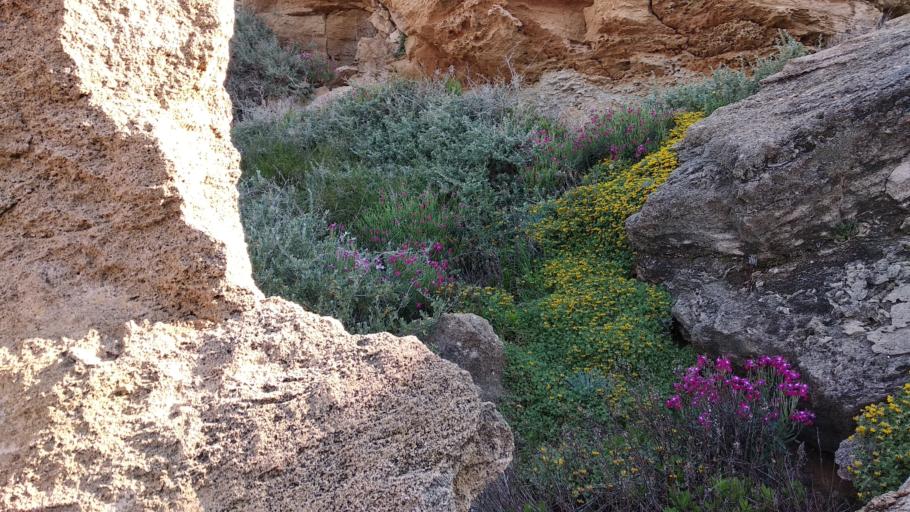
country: IT
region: Calabria
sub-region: Provincia di Crotone
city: Le Castella
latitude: 38.9061
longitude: 17.0216
